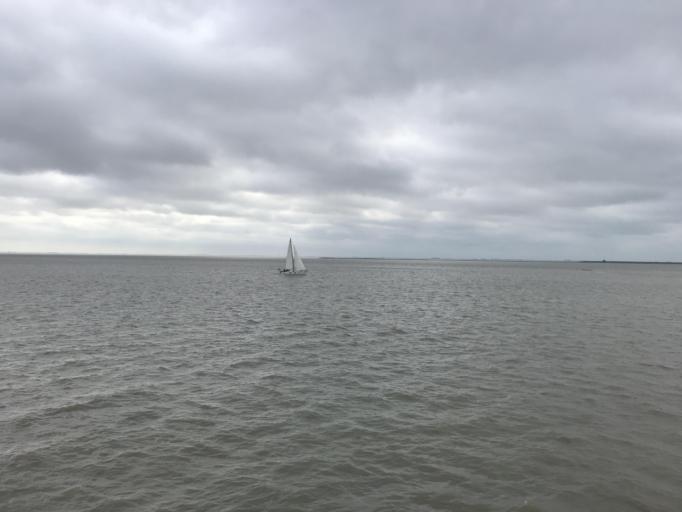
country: DE
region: Lower Saxony
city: Emden
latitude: 53.3271
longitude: 7.0796
